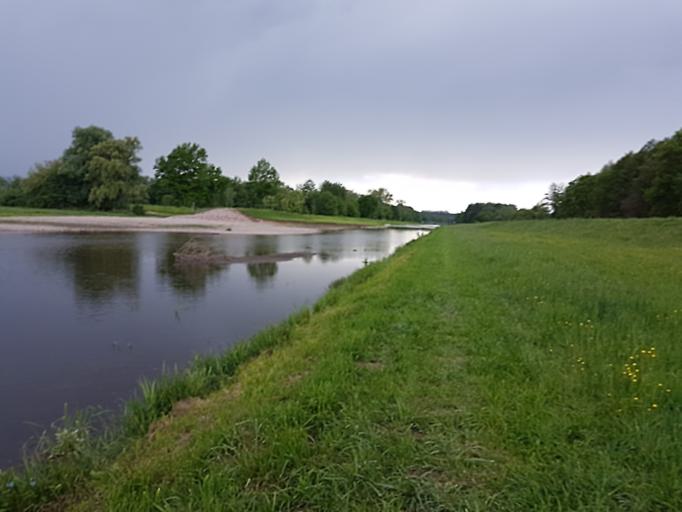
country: DE
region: Baden-Wuerttemberg
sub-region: Freiburg Region
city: Teningen
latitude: 48.1392
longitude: 7.7879
